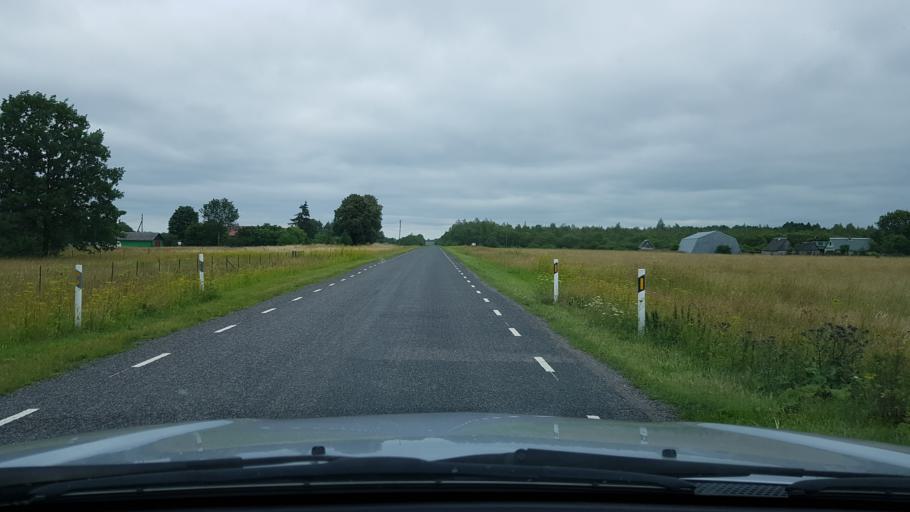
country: EE
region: Ida-Virumaa
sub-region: Narva linn
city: Narva
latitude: 59.3739
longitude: 28.1079
